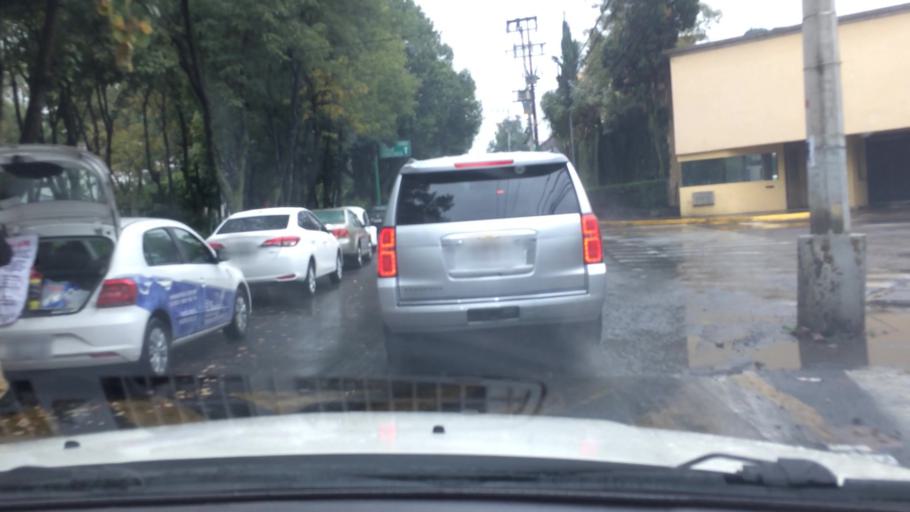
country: MX
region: Mexico City
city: Magdalena Contreras
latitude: 19.3157
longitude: -99.2131
